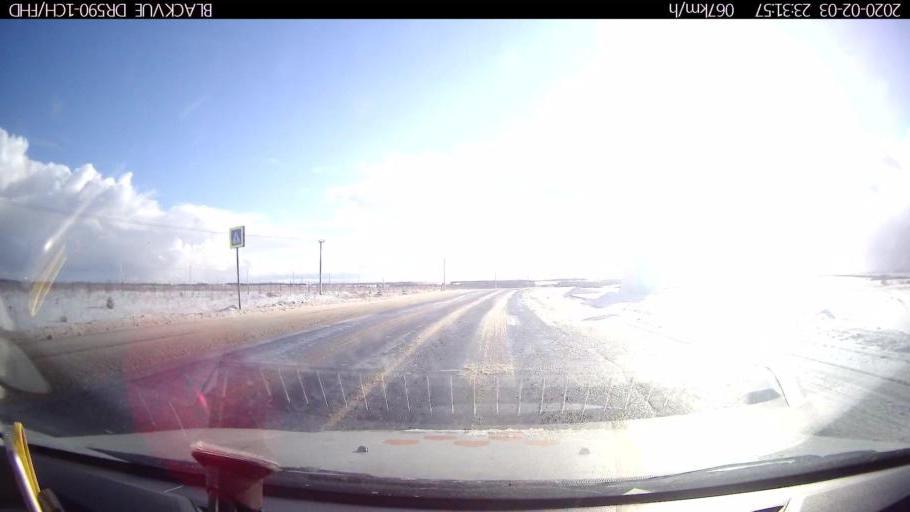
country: RU
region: Nizjnij Novgorod
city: Dal'neye Konstantinovo
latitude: 55.9369
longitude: 44.2300
